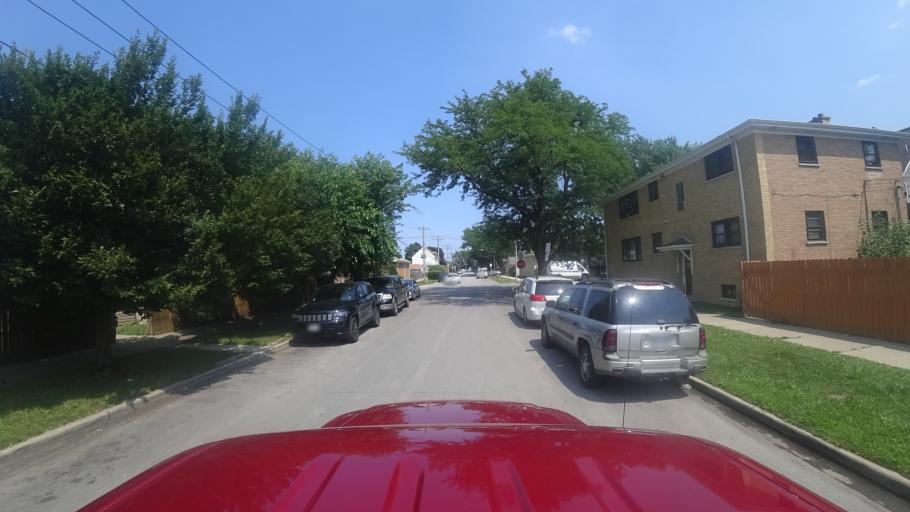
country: US
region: Illinois
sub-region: Cook County
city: Cicero
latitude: 41.7986
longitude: -87.7312
